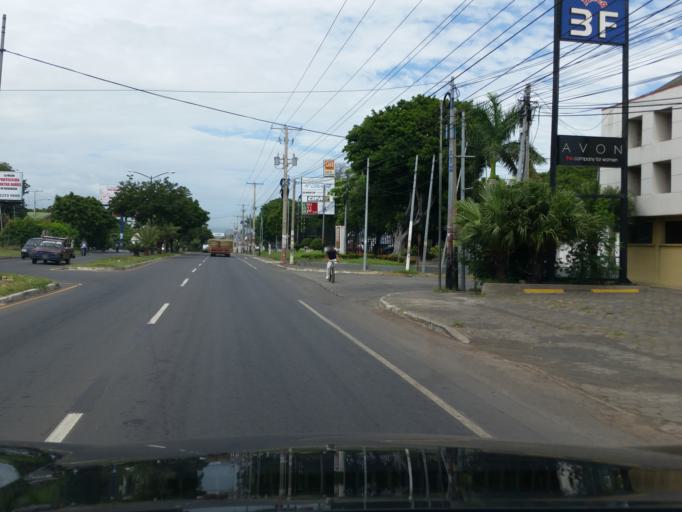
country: NI
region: Managua
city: Managua
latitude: 12.1510
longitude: -86.2271
